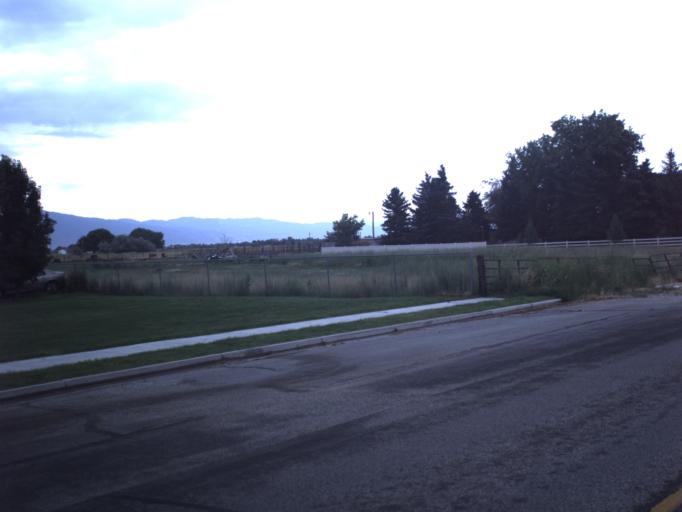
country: US
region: Utah
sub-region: Davis County
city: West Point
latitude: 41.1136
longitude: -112.1126
